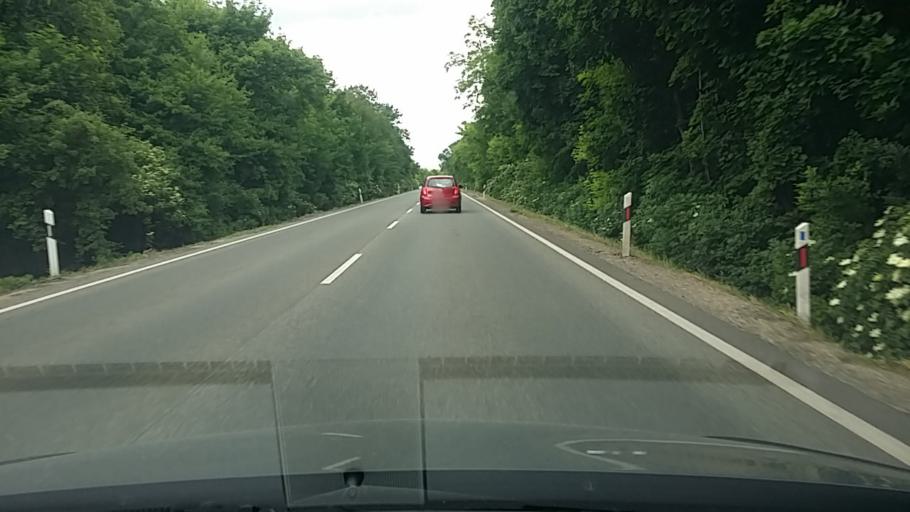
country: HU
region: Fejer
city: dunaujvaros
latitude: 46.9641
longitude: 18.9086
